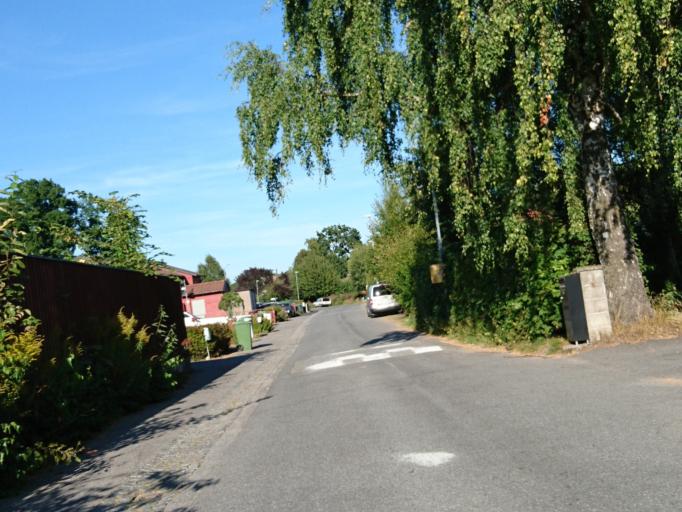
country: SE
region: Stockholm
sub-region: Huddinge Kommun
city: Segeltorp
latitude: 59.2765
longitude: 17.9331
